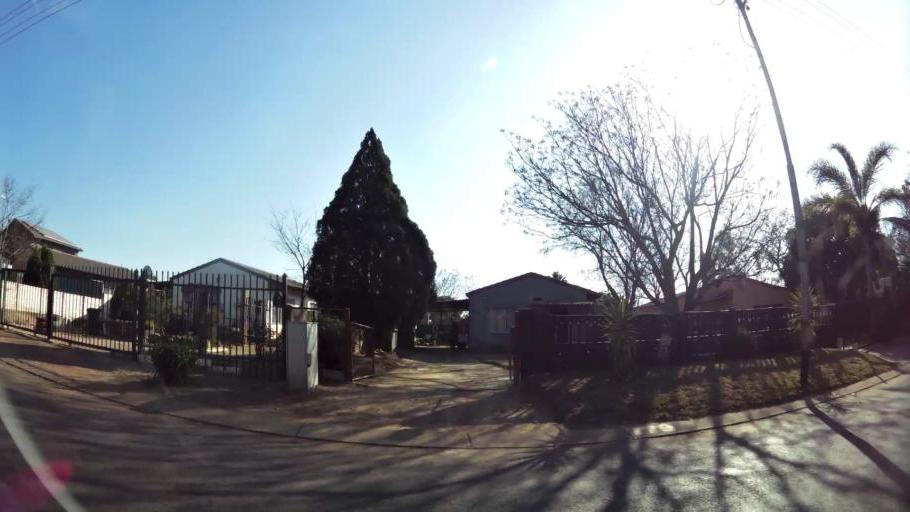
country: ZA
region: Gauteng
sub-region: City of Tshwane Metropolitan Municipality
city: Pretoria
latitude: -25.7110
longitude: 28.1395
